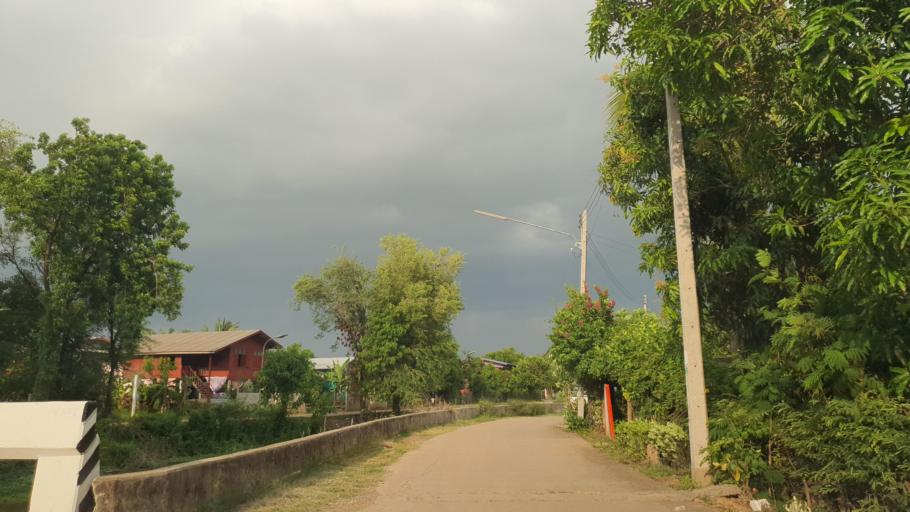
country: TH
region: Sukhothai
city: Ban Na
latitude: 17.0134
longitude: 99.7764
